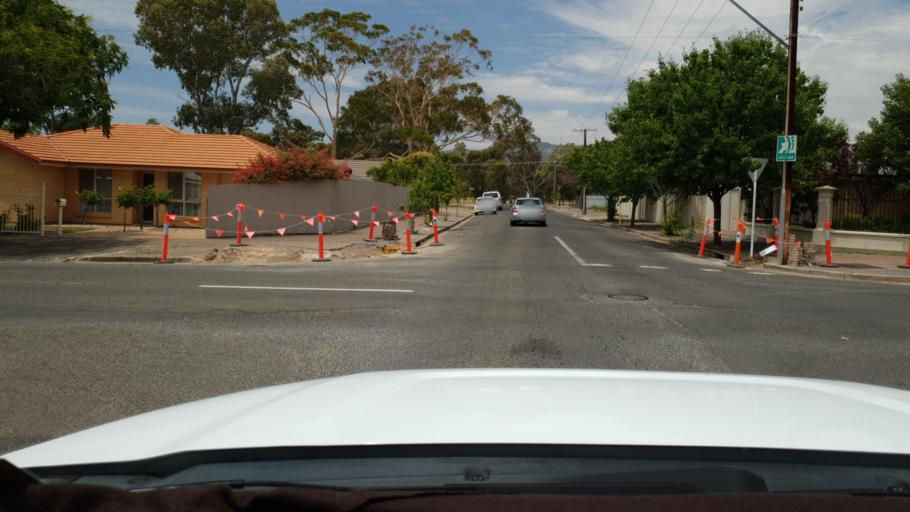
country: AU
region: South Australia
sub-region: Marion
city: Clovelly Park
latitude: -34.9986
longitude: 138.5789
